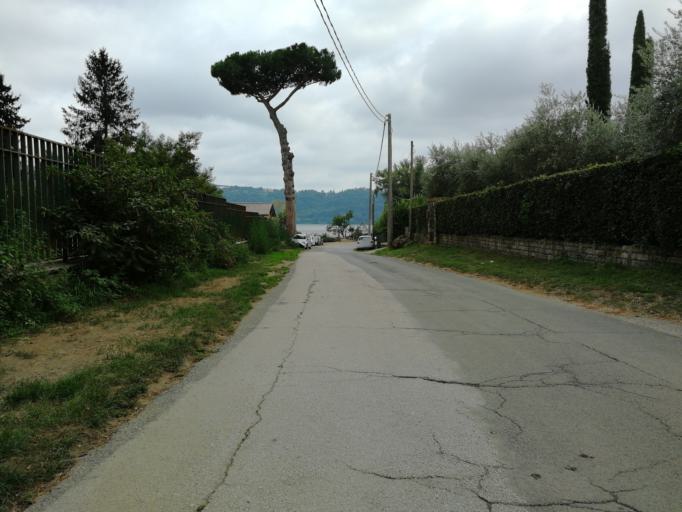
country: IT
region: Latium
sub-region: Citta metropolitana di Roma Capitale
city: Nemi
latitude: 41.7223
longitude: 12.7012
